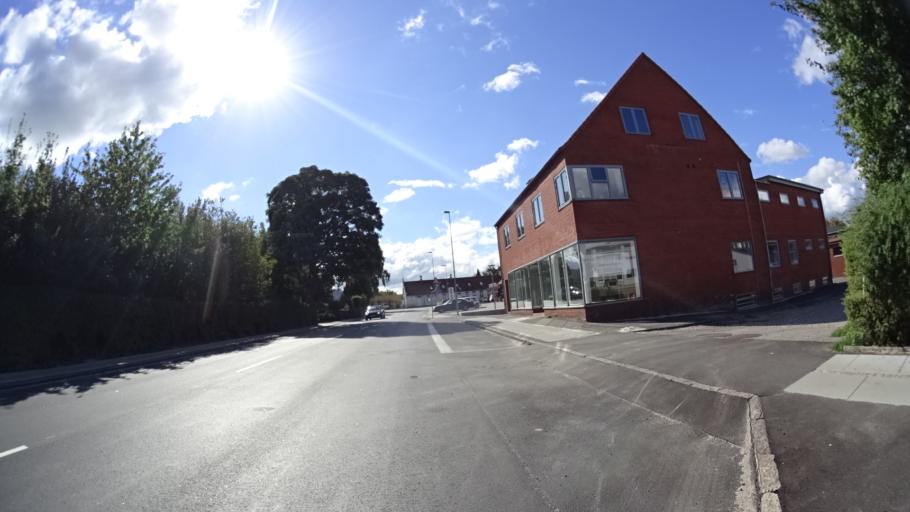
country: DK
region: Central Jutland
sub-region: Arhus Kommune
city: Marslet
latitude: 56.1150
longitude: 10.1743
